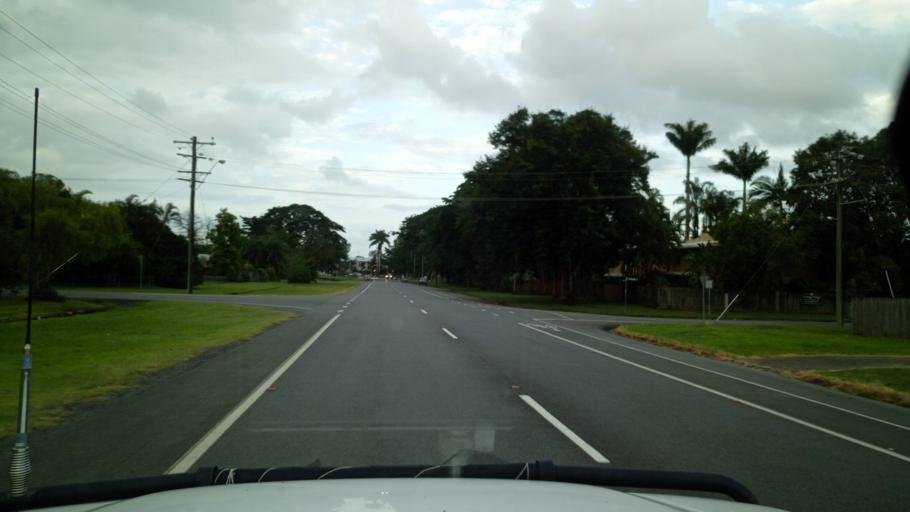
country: AU
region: Queensland
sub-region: Cairns
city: Woree
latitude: -16.9300
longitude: 145.7396
